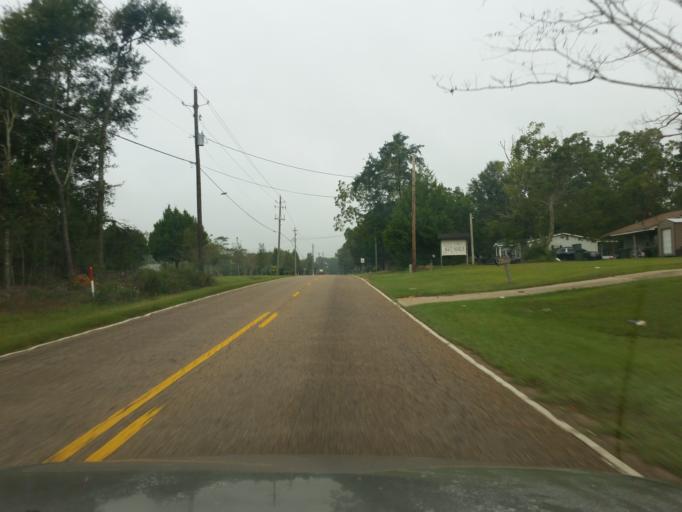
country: US
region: Florida
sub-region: Escambia County
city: Cantonment
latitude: 30.6059
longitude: -87.3475
